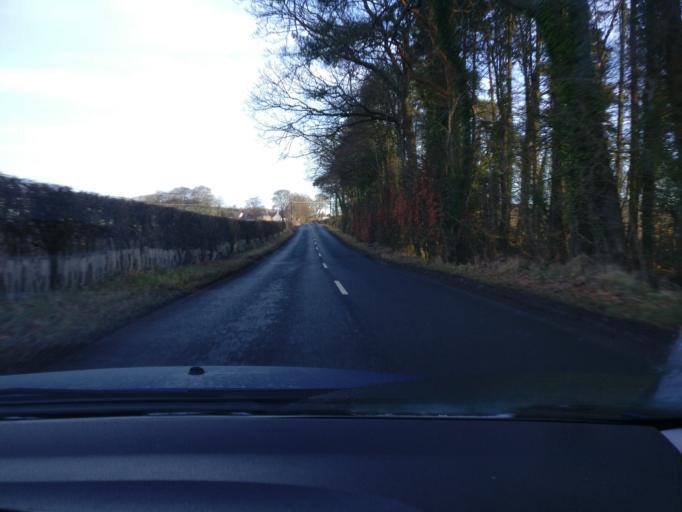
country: GB
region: Scotland
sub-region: The Scottish Borders
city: Hawick
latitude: 55.4460
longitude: -2.7650
